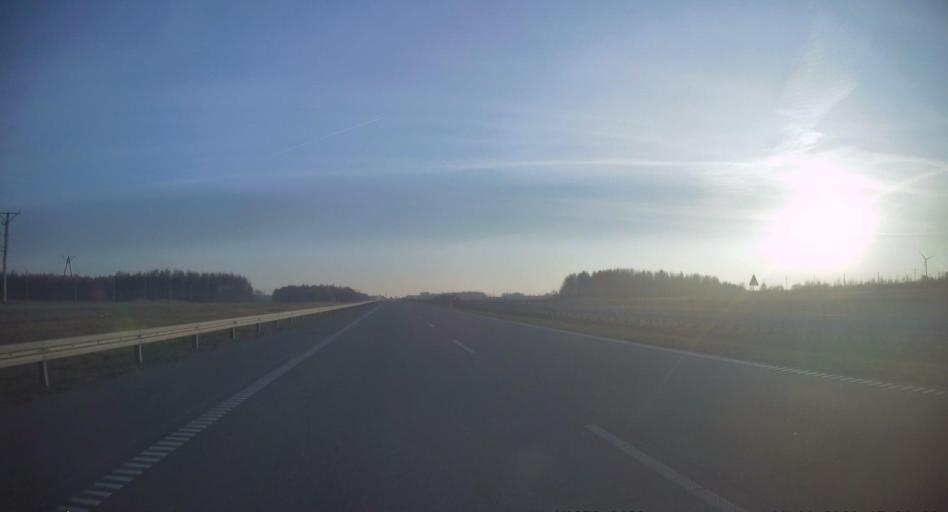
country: PL
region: Silesian Voivodeship
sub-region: Powiat czestochowski
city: Starcza
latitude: 50.6376
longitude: 19.0355
